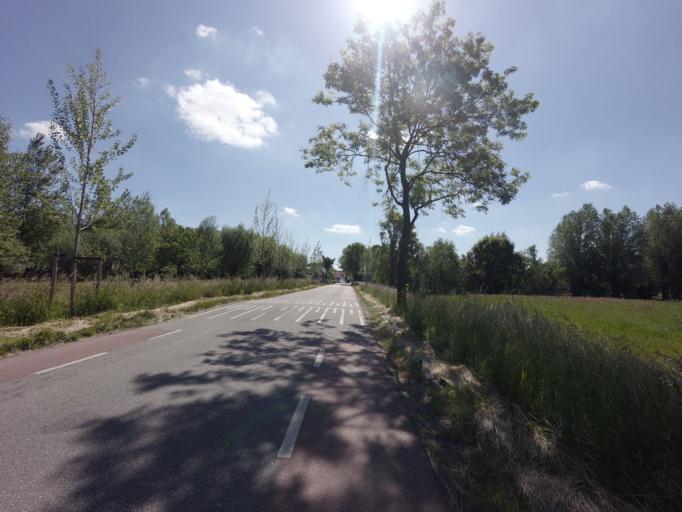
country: NL
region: Utrecht
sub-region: Gemeente IJsselstein
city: IJsselstein
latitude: 52.0470
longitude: 5.0446
